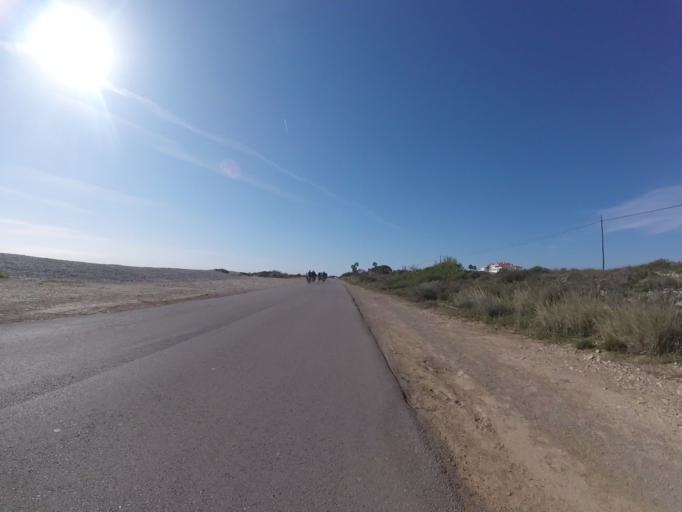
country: ES
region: Valencia
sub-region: Provincia de Castello
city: Alcoceber
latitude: 40.2156
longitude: 0.2665
